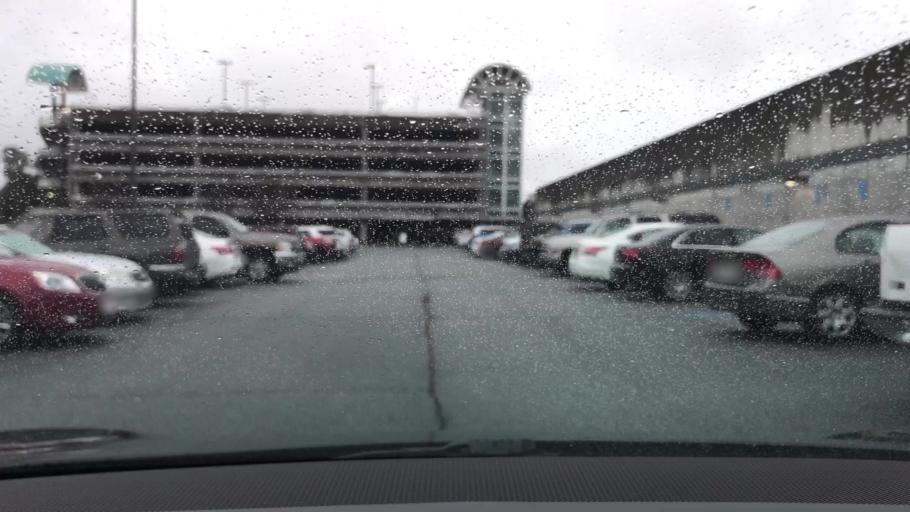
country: US
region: Georgia
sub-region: DeKalb County
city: Doraville
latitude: 33.9021
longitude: -84.2812
